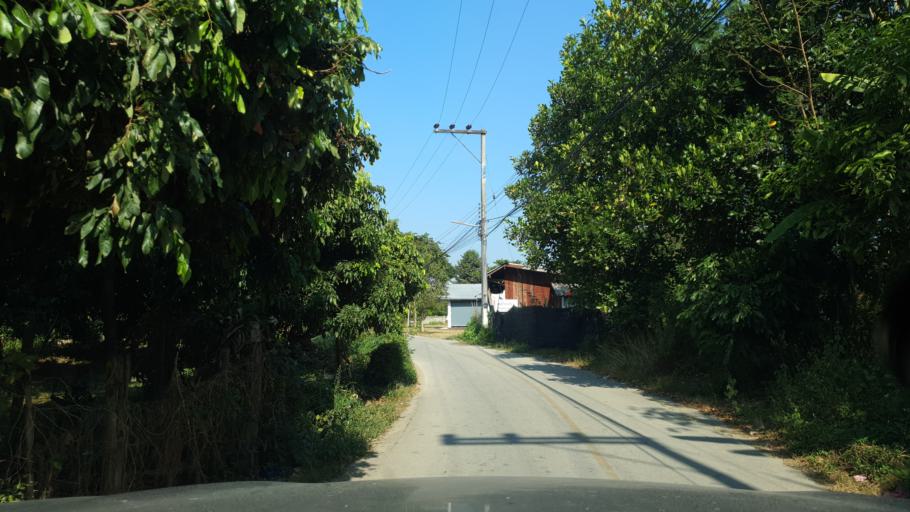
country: TH
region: Chiang Mai
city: Saraphi
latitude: 18.7181
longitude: 99.0720
